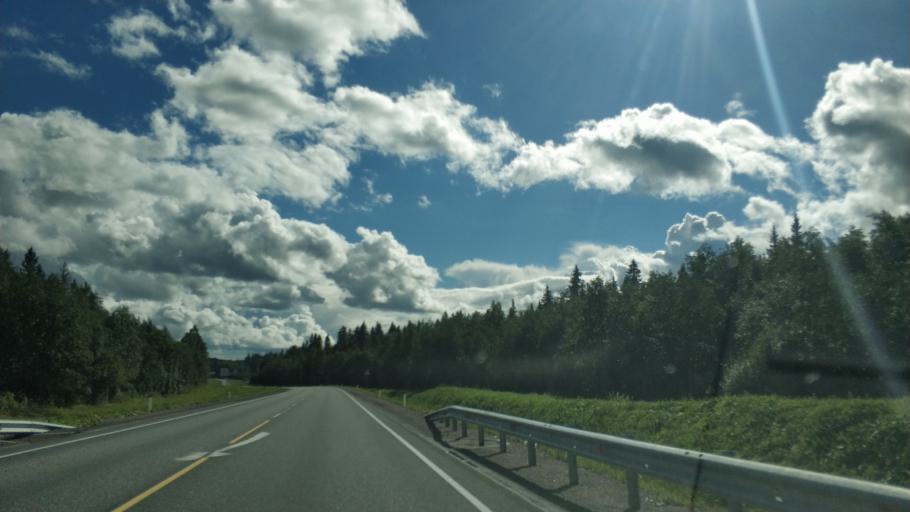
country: RU
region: Republic of Karelia
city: Ruskeala
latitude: 61.8796
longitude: 30.6442
